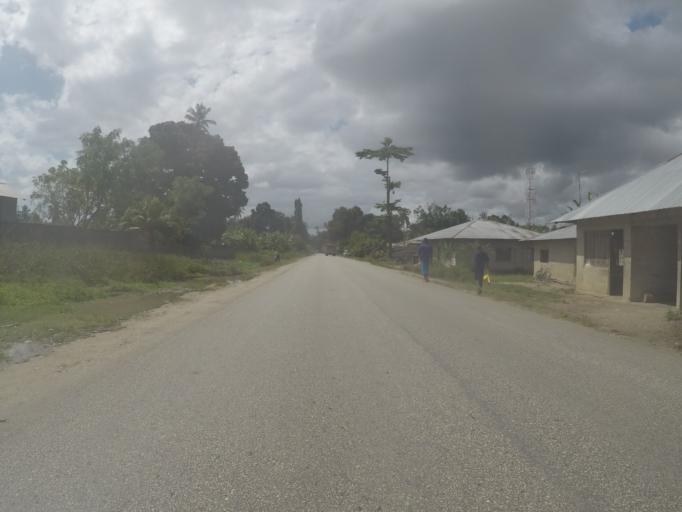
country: TZ
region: Zanzibar North
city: Gamba
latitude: -5.9876
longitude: 39.2516
